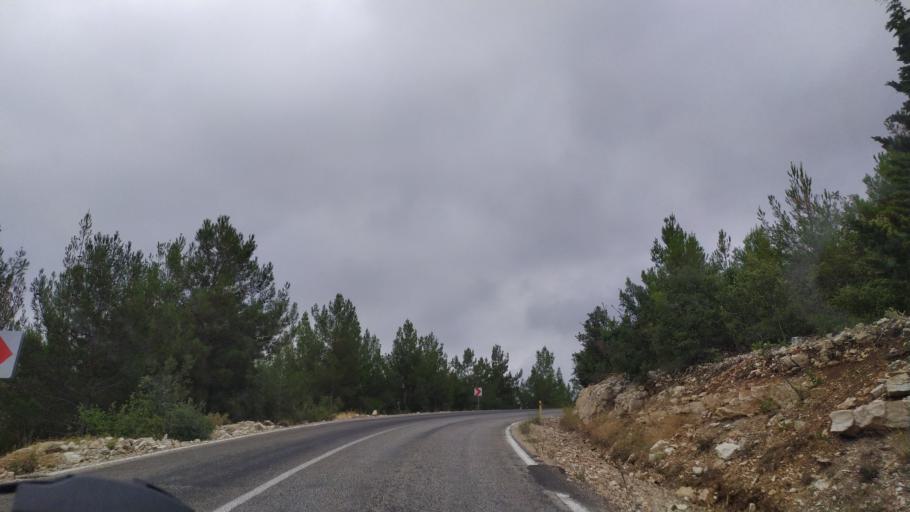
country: TR
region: Mersin
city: Silifke
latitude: 36.5413
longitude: 33.9300
